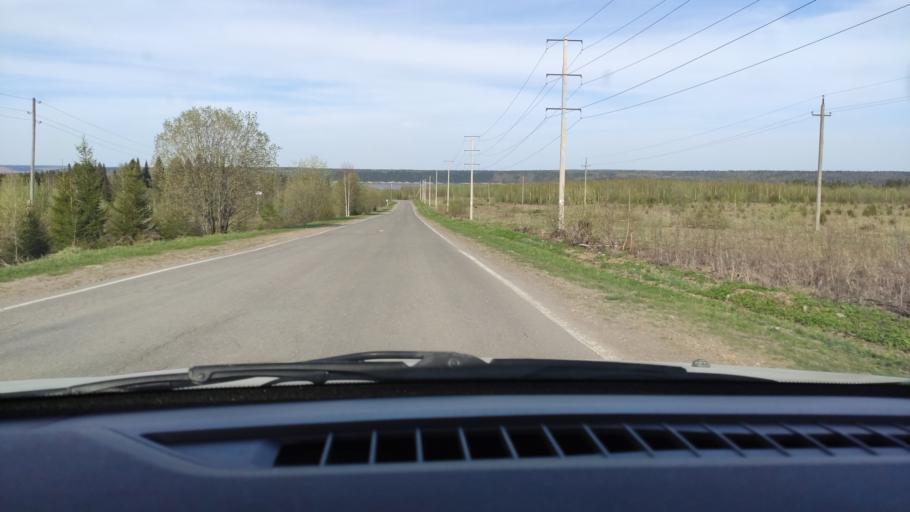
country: RU
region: Perm
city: Sylva
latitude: 57.9226
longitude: 56.6771
